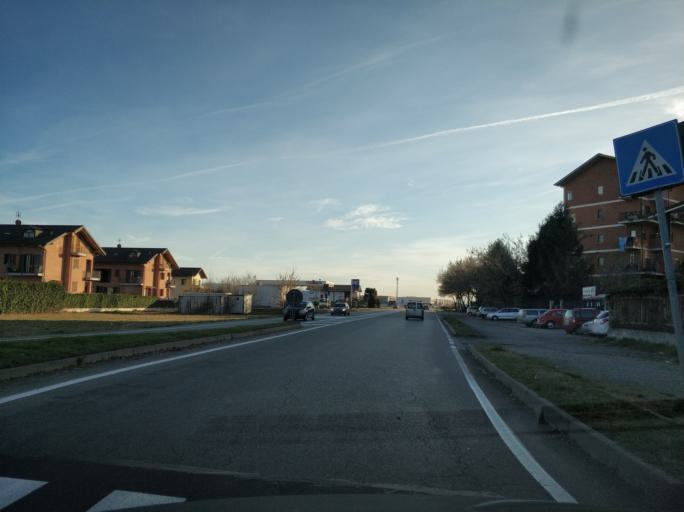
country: IT
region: Piedmont
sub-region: Provincia di Torino
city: Volpiano
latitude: 45.1961
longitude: 7.7889
